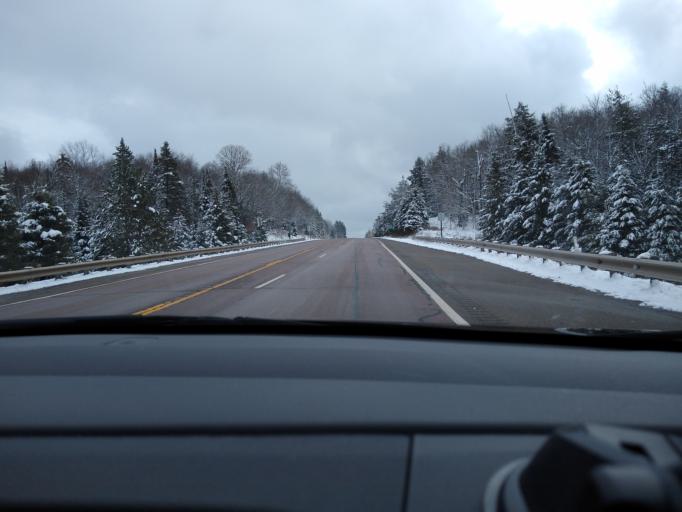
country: US
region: Michigan
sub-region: Iron County
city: Iron River
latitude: 46.1920
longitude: -88.9929
